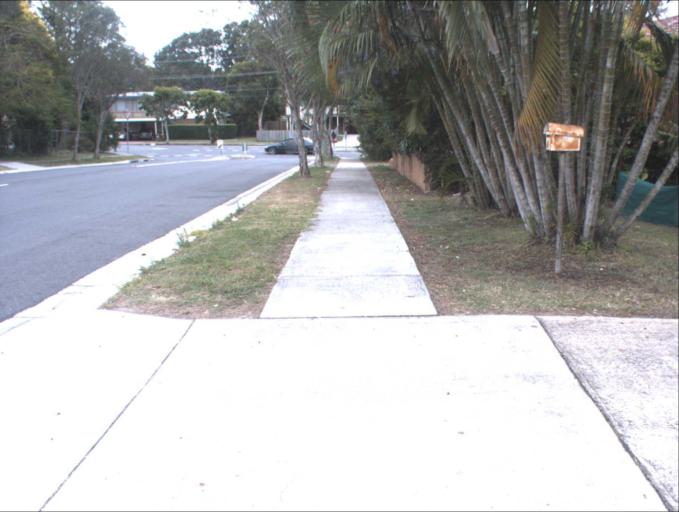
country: AU
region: Queensland
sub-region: Logan
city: Logan City
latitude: -27.6556
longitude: 153.1124
